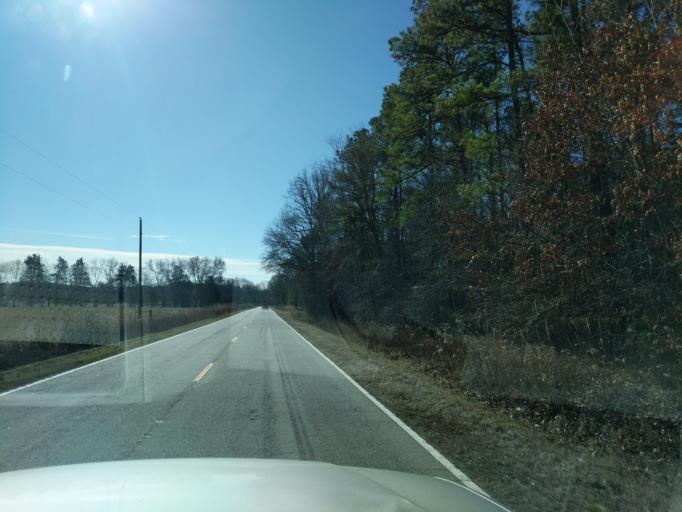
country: US
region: South Carolina
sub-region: Laurens County
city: Joanna
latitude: 34.2953
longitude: -81.8445
